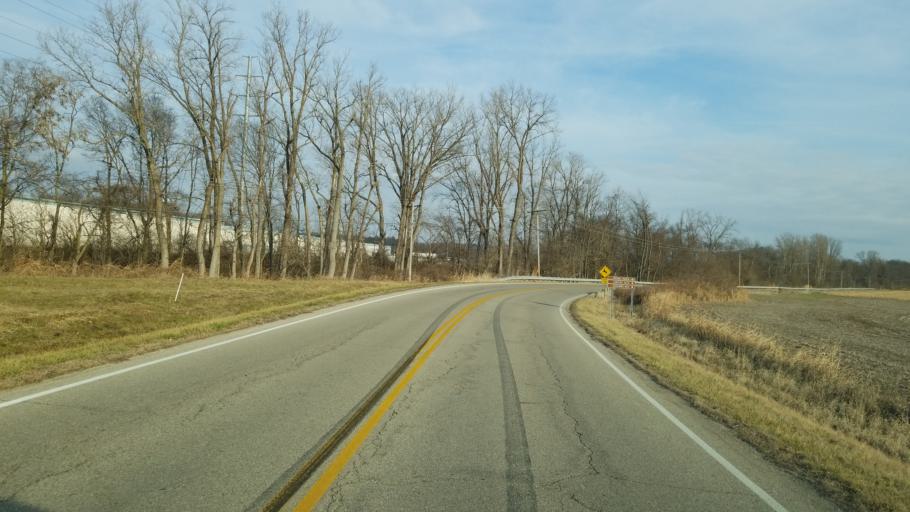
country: US
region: Ohio
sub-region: Ross County
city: Chillicothe
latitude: 39.3864
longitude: -82.9629
